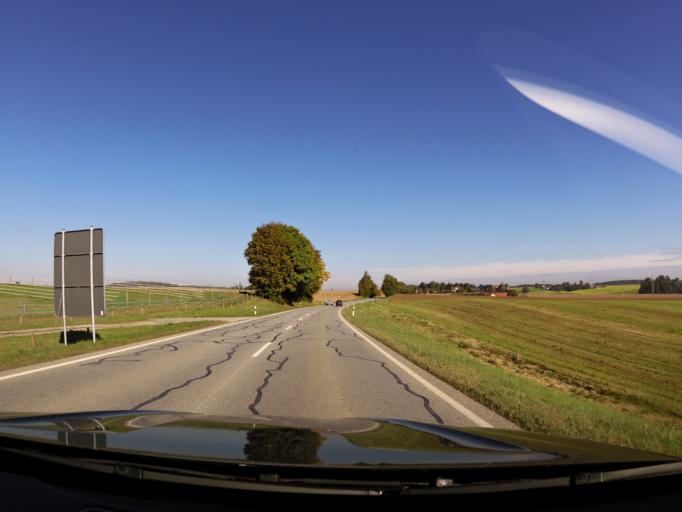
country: DE
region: Bavaria
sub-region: Lower Bavaria
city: Altfraunhofen
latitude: 48.4578
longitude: 12.1495
